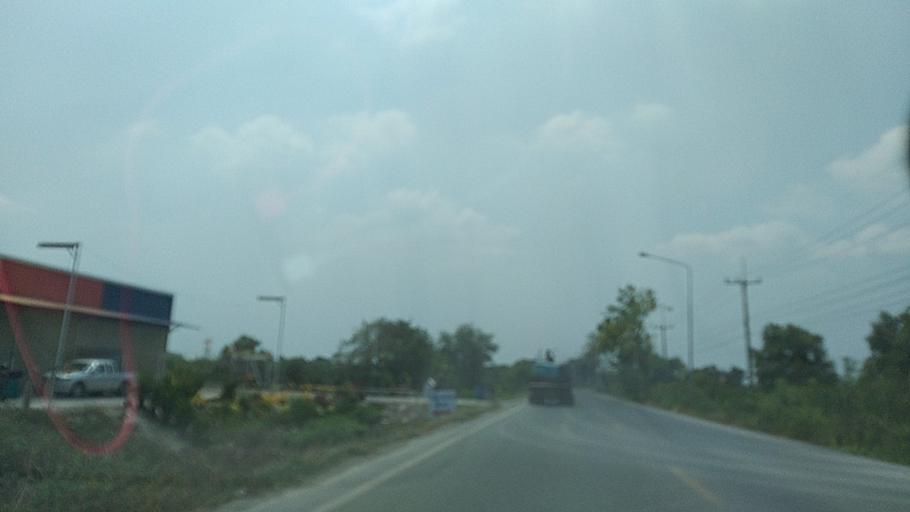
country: TH
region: Pathum Thani
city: Ban Lam Luk Ka
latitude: 13.9824
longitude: 100.8414
